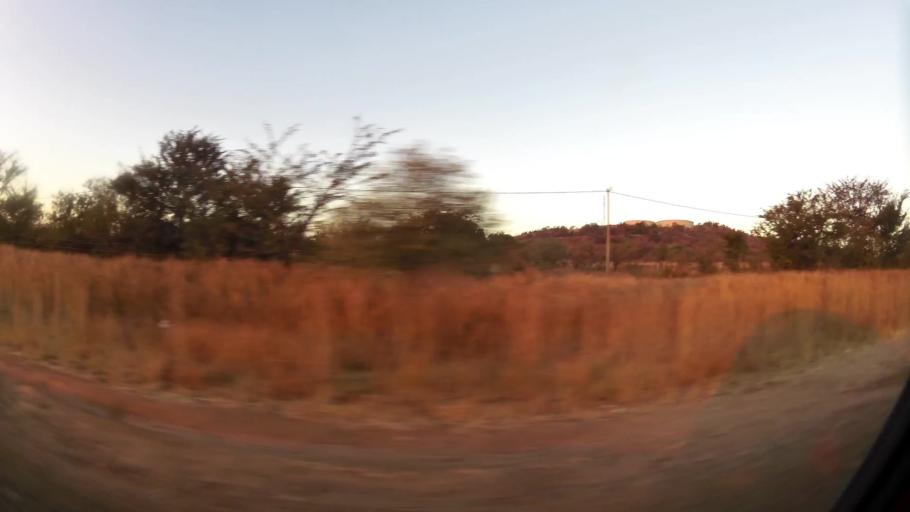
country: ZA
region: North-West
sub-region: Bojanala Platinum District Municipality
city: Rustenburg
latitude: -25.6166
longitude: 27.1798
